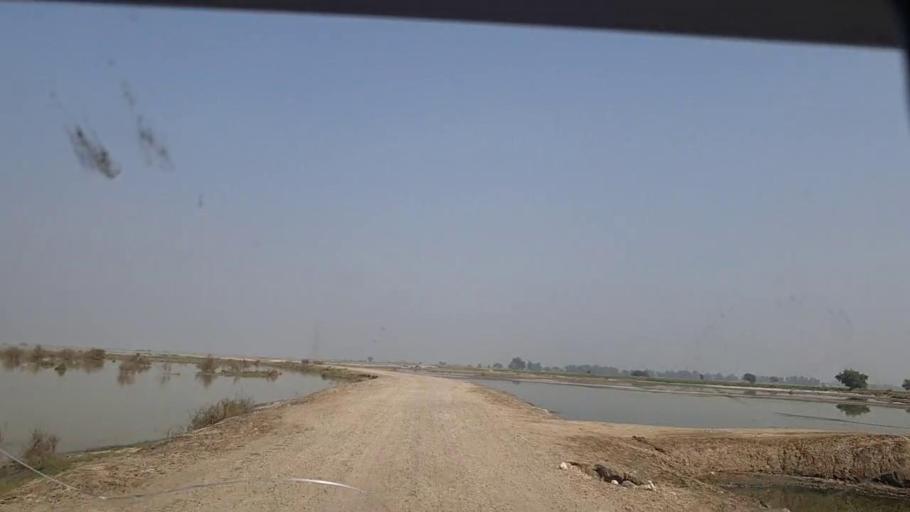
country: PK
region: Sindh
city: Shikarpur
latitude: 28.0420
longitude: 68.6503
